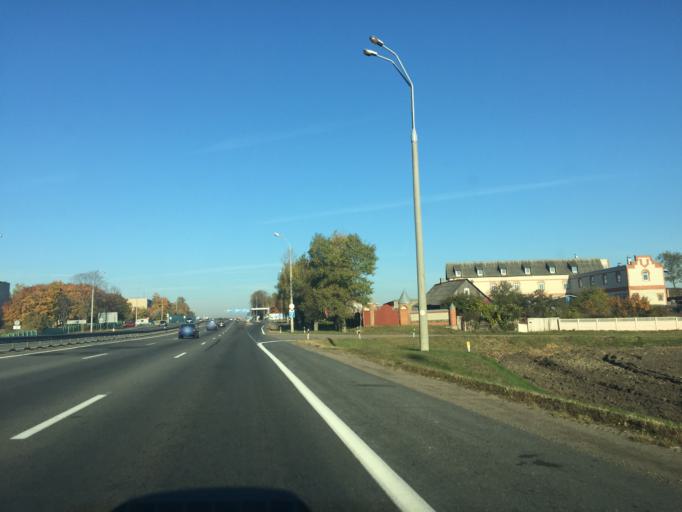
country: BY
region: Minsk
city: Pryvol'ny
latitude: 53.7978
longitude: 27.8085
